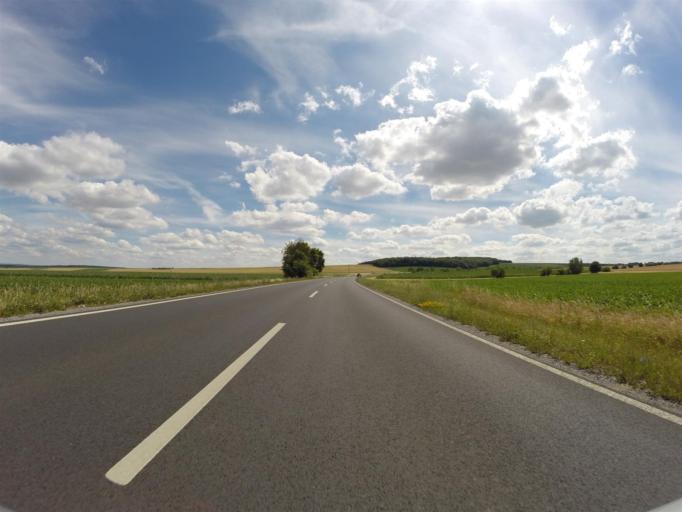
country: DE
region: Bavaria
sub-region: Regierungsbezirk Unterfranken
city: Kolitzheim
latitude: 49.9090
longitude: 10.2373
